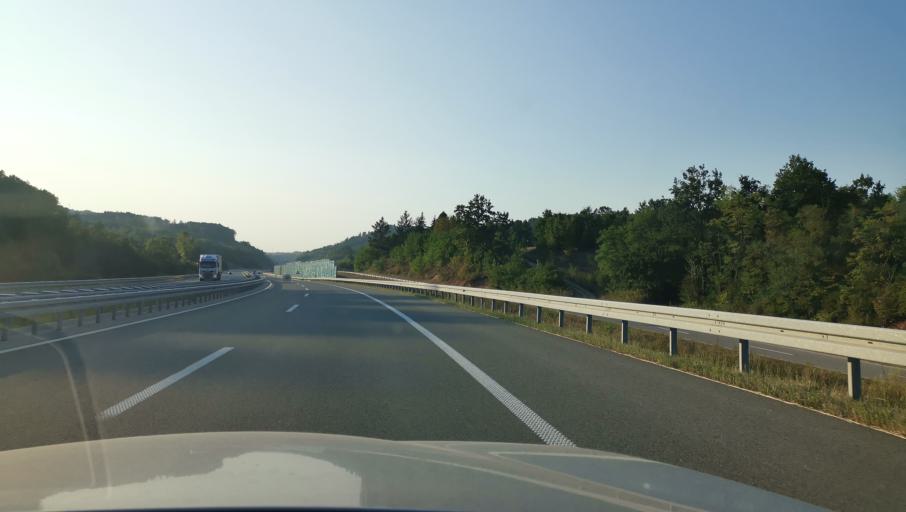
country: RS
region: Central Serbia
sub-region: Moravicki Okrug
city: Gornji Milanovac
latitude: 44.1261
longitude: 20.3664
